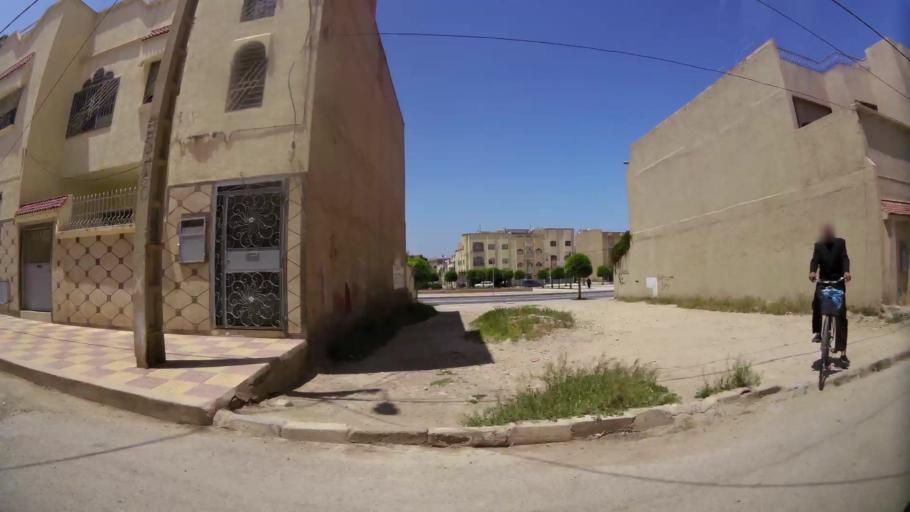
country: MA
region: Oriental
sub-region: Oujda-Angad
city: Oujda
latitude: 34.7007
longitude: -1.8971
